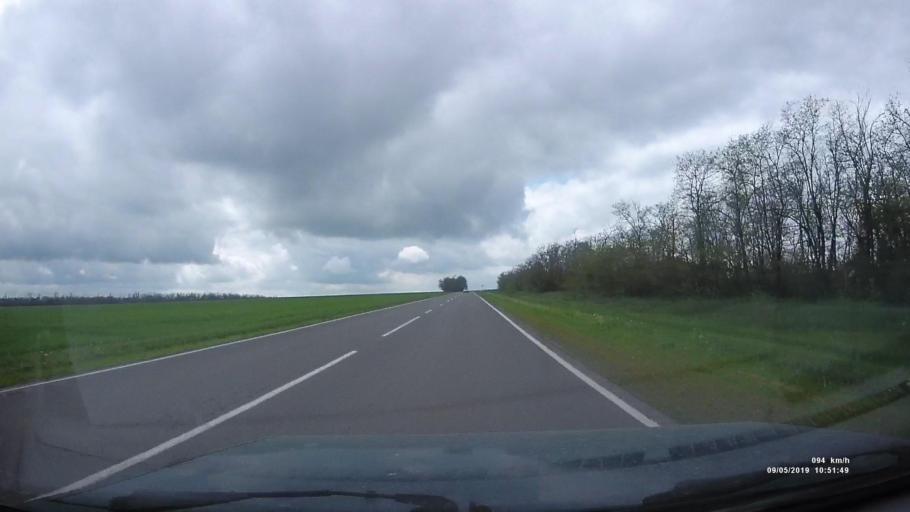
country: RU
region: Rostov
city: Peshkovo
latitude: 46.9088
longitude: 39.3541
